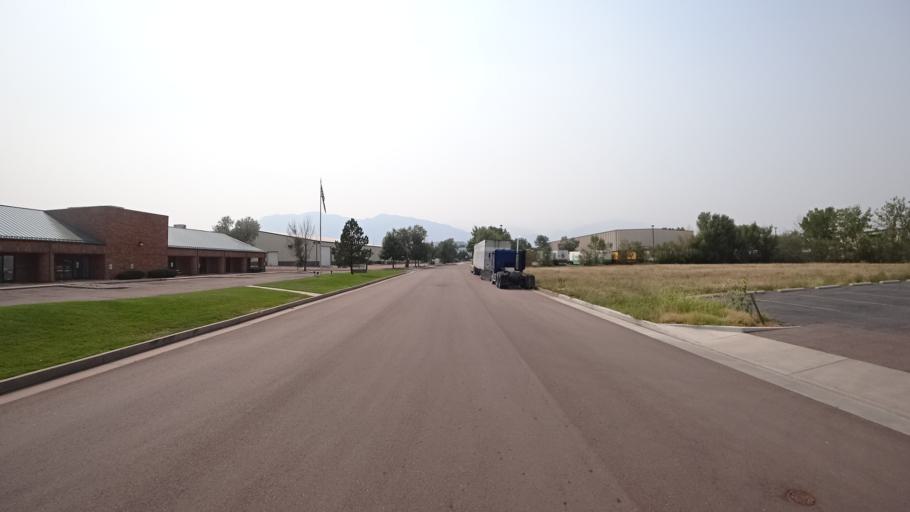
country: US
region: Colorado
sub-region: El Paso County
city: Stratmoor
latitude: 38.7900
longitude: -104.7869
